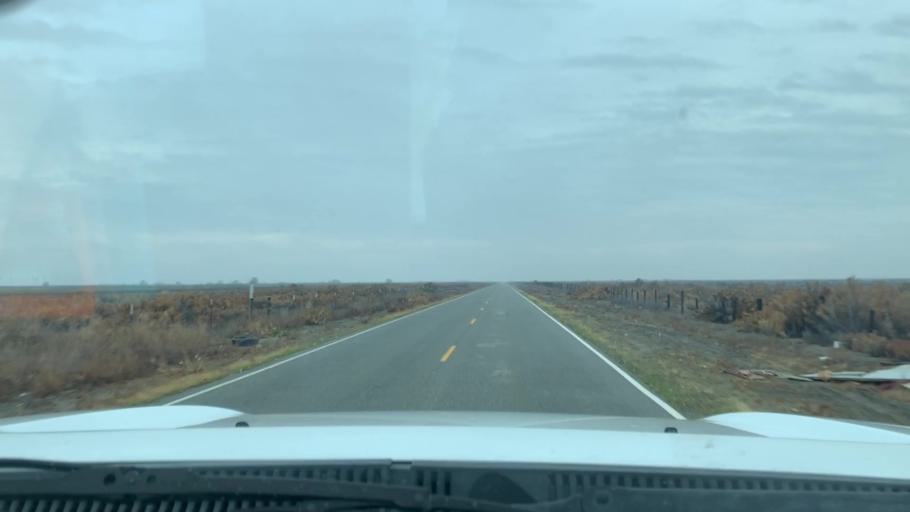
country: US
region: California
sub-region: Kern County
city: Lost Hills
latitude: 35.7355
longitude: -119.5794
